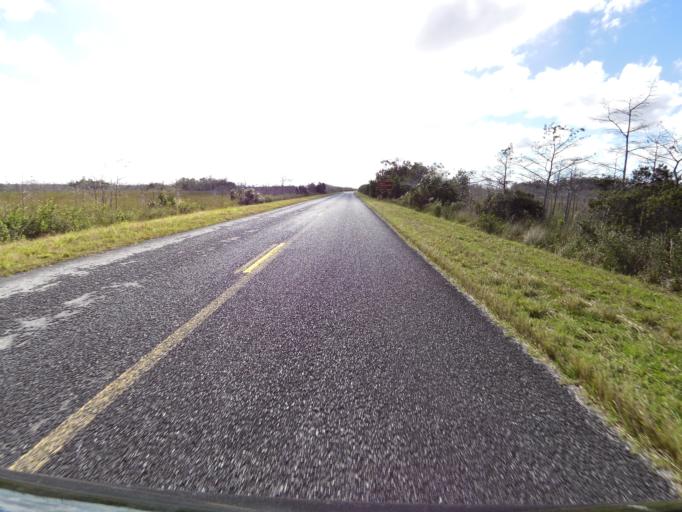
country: US
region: Florida
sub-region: Miami-Dade County
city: Florida City
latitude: 25.4109
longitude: -80.7840
